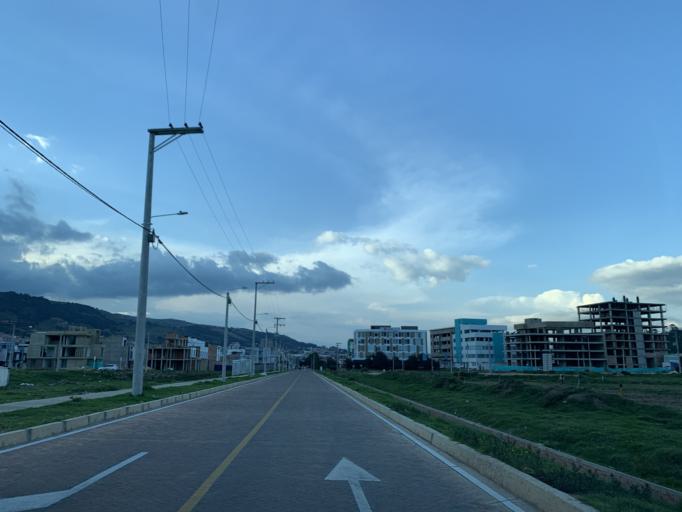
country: CO
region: Boyaca
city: Tunja
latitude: 5.5502
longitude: -73.3478
